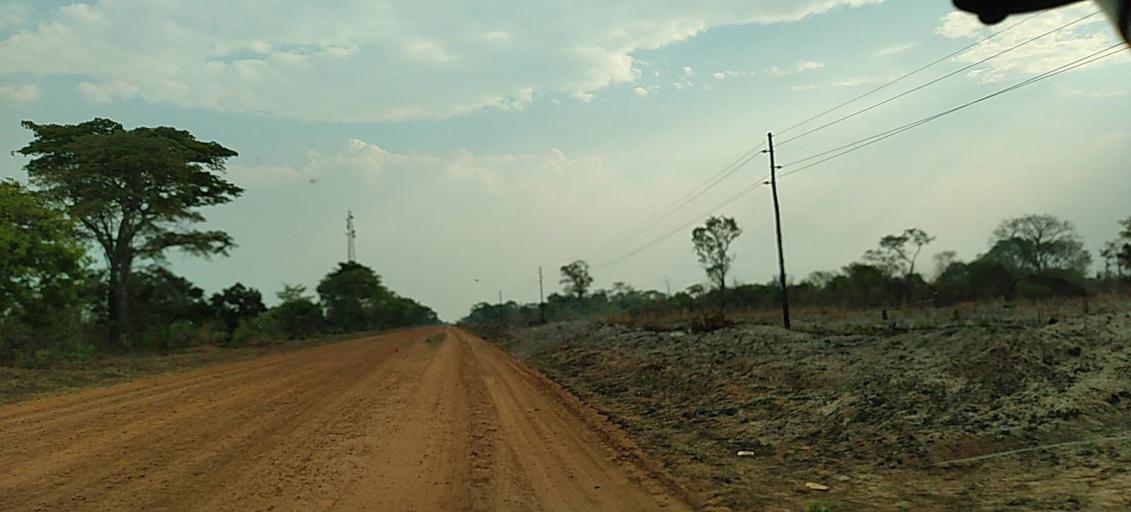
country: ZM
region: North-Western
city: Kabompo
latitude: -13.8816
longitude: 23.6636
